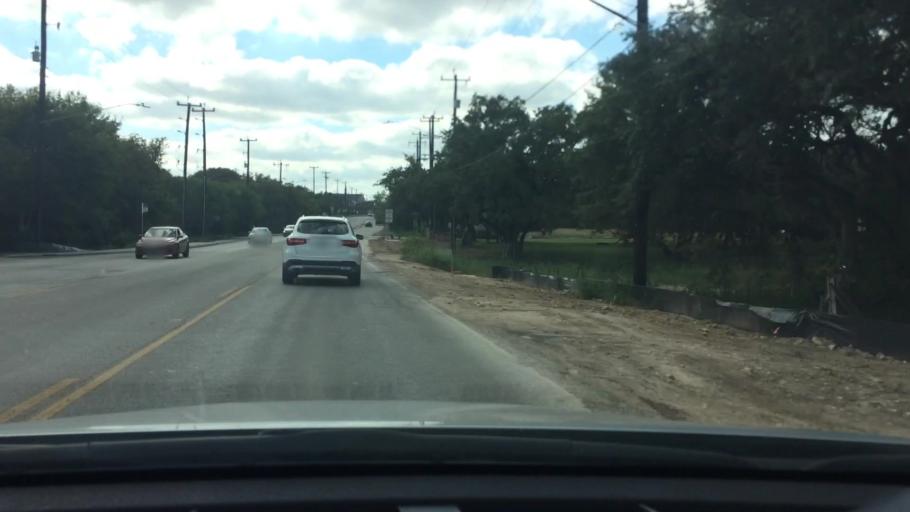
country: US
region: Texas
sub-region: Bexar County
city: Shavano Park
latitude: 29.5694
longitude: -98.5762
